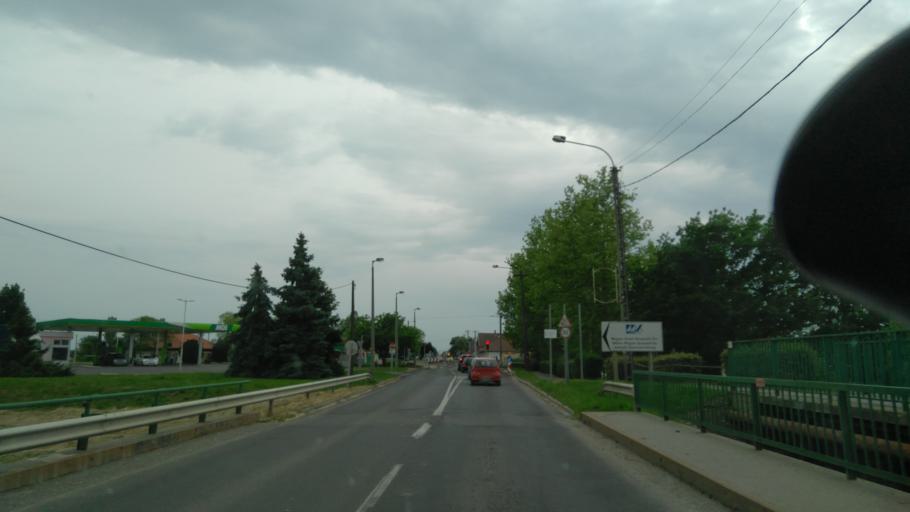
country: HU
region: Bekes
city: Sarkad
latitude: 46.7401
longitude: 21.3754
